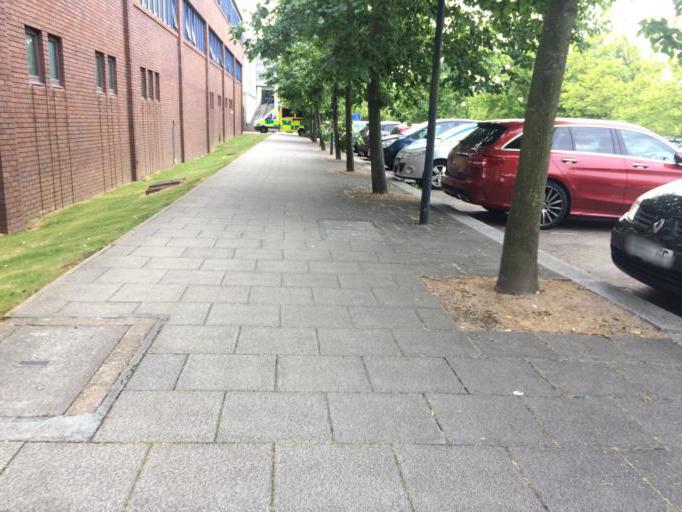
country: GB
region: England
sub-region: Milton Keynes
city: Milton Keynes
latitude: 52.0415
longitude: -0.7674
